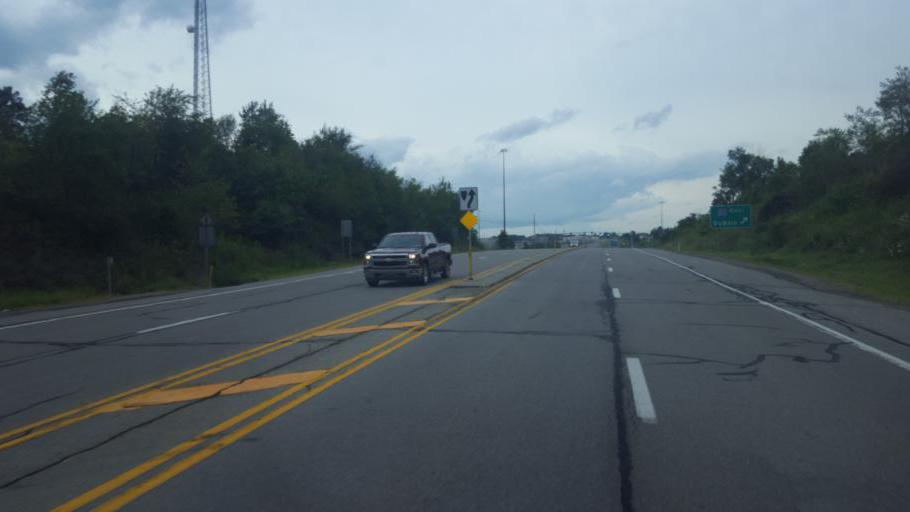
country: US
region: Pennsylvania
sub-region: Clarion County
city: Clarion
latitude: 41.1826
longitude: -79.3949
